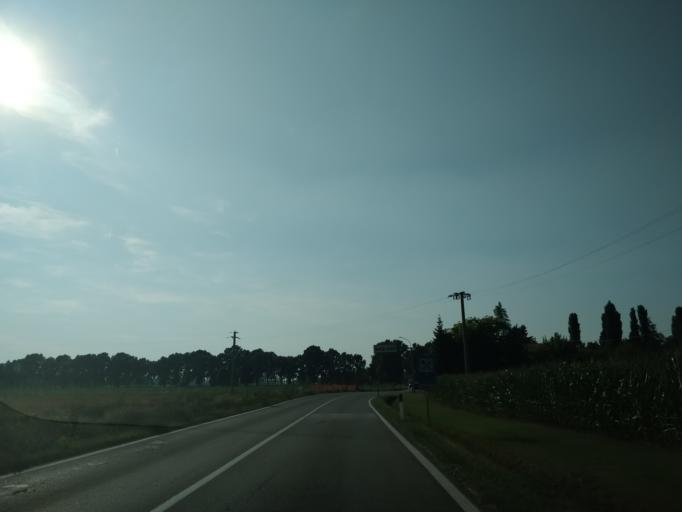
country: IT
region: Emilia-Romagna
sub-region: Provincia di Bologna
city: Castello d'Argile
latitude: 44.6639
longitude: 11.3101
